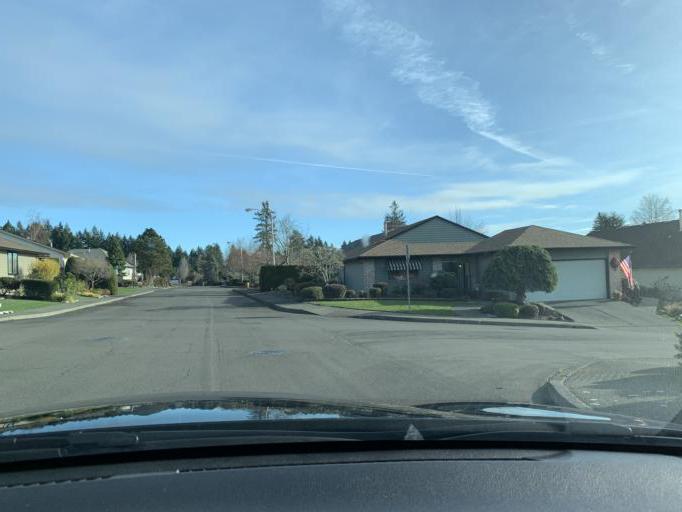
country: US
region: Washington
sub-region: Clark County
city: Mill Plain
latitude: 45.5988
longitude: -122.5152
